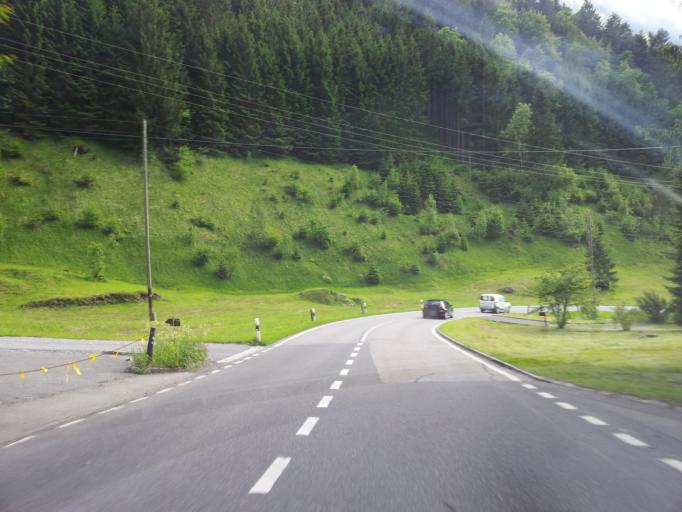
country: CH
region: Bern
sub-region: Interlaken-Oberhasli District
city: Lauterbrunnen
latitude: 46.6367
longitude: 7.9649
